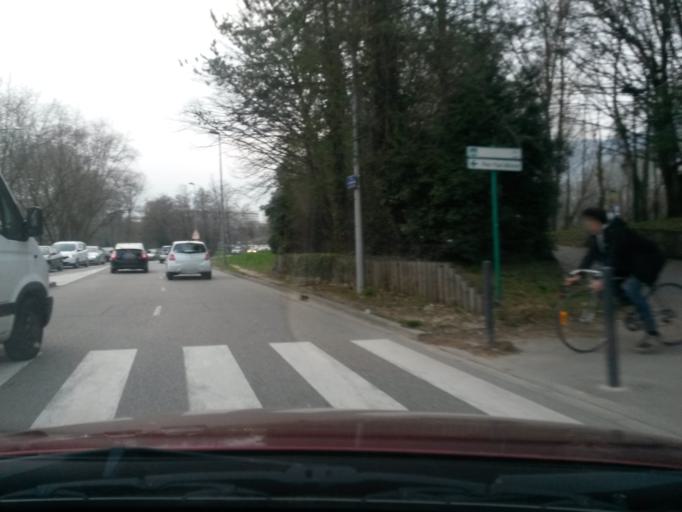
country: FR
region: Rhone-Alpes
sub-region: Departement de l'Isere
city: La Tronche
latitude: 45.1882
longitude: 5.7460
